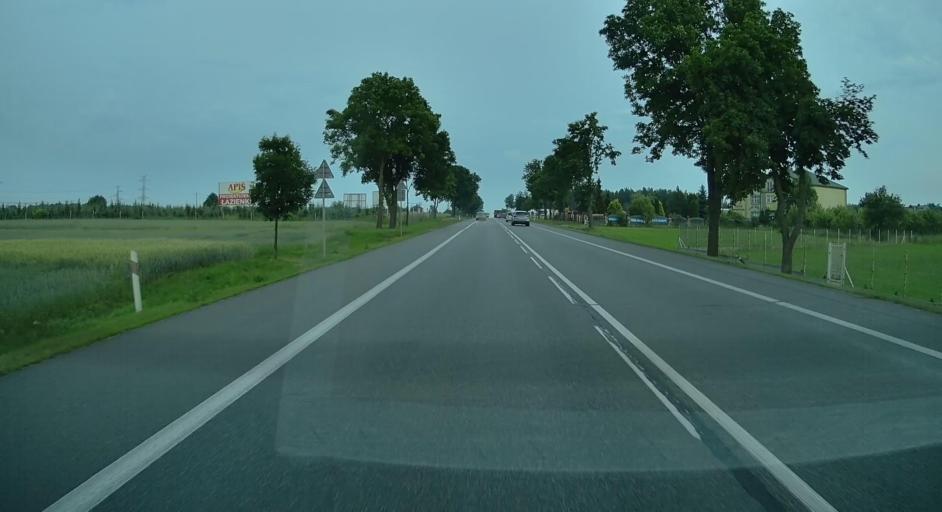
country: PL
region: Masovian Voivodeship
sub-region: Siedlce
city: Siedlce
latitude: 52.1273
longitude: 22.3408
